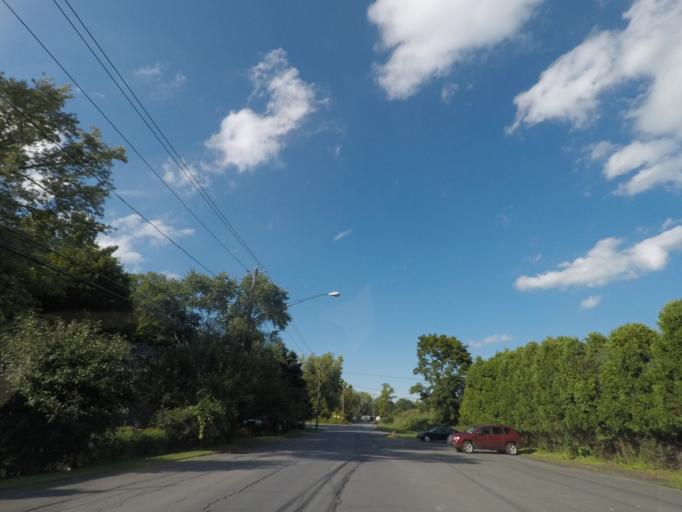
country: US
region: New York
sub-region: Albany County
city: Watervliet
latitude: 42.7394
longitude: -73.7114
